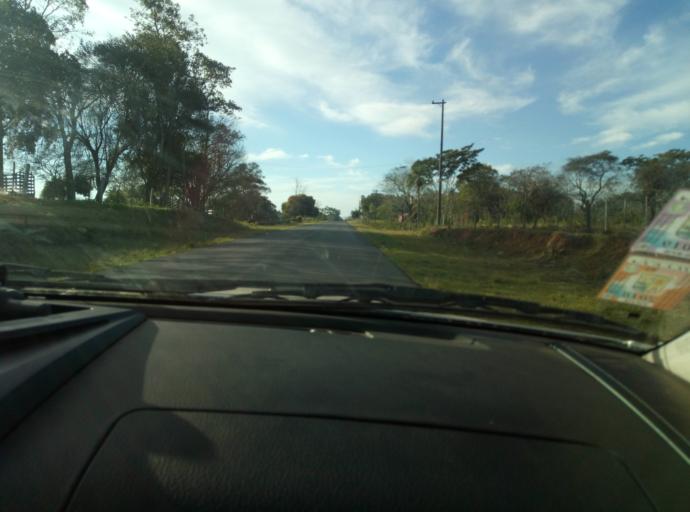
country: PY
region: Caaguazu
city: Carayao
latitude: -25.1608
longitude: -56.3121
